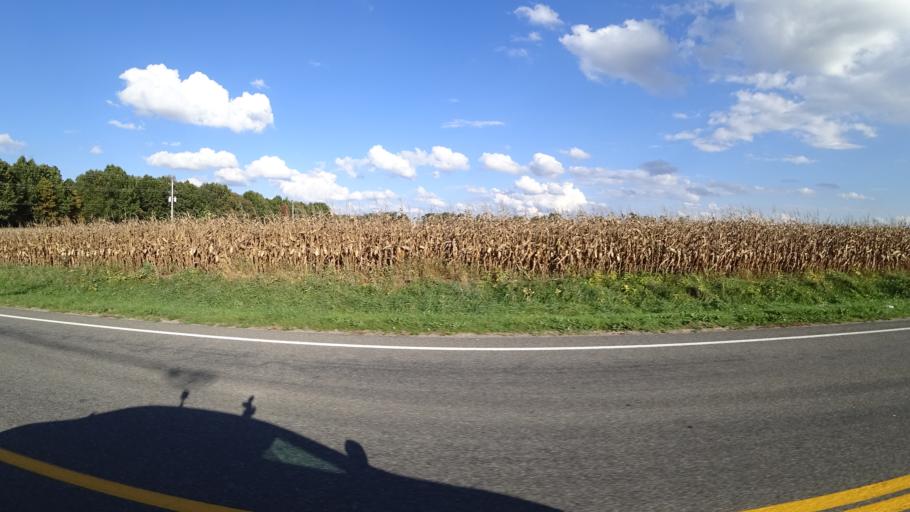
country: US
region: Michigan
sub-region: Saint Joseph County
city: Centreville
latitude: 41.8678
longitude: -85.5068
